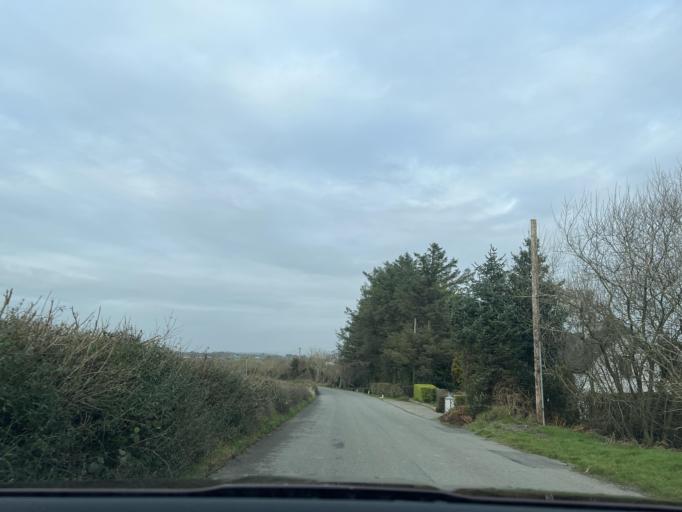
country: IE
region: Leinster
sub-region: Loch Garman
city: Castlebridge
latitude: 52.3801
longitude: -6.5481
